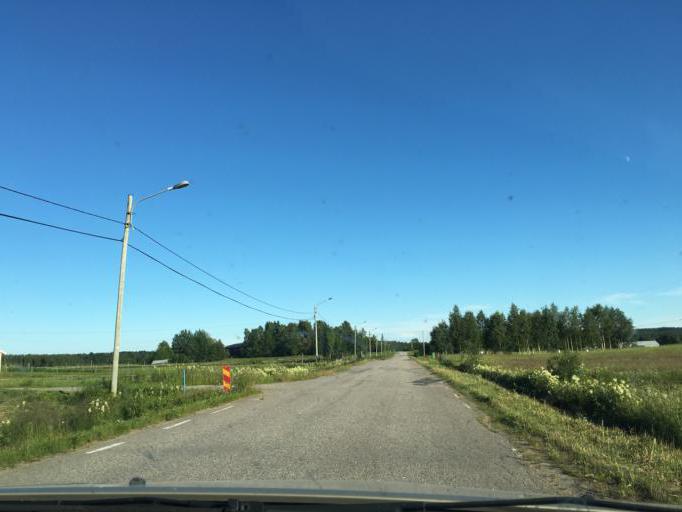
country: SE
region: Norrbotten
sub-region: Kalix Kommun
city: Rolfs
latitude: 65.8968
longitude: 22.9390
